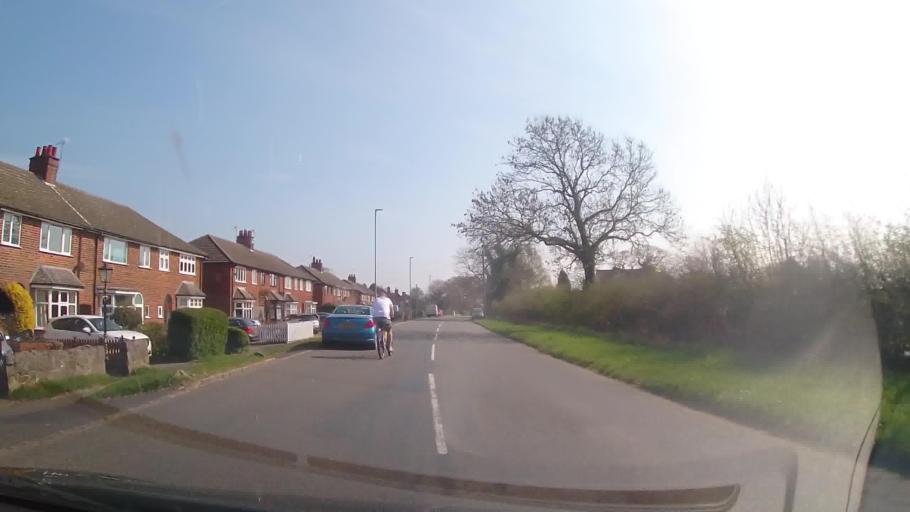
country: GB
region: England
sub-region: Leicestershire
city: Anstey
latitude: 52.6783
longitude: -1.2037
